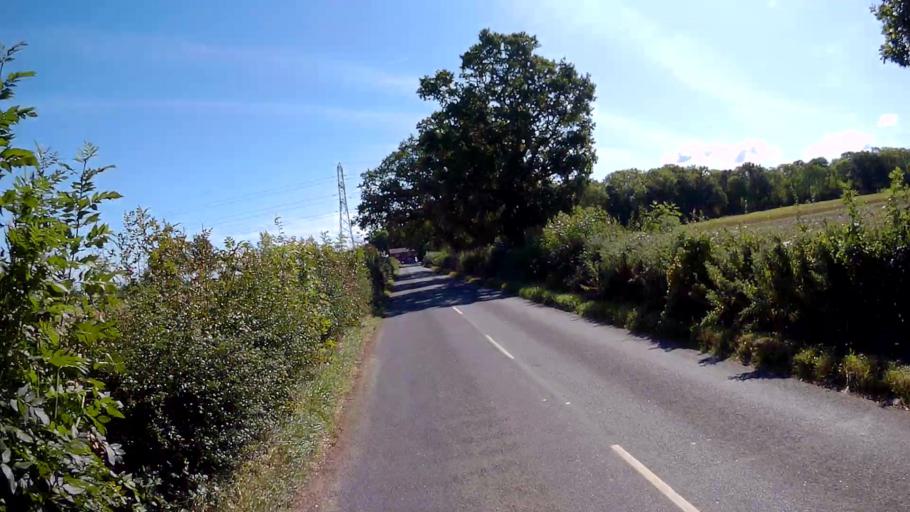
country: GB
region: England
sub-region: West Berkshire
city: Stratfield Mortimer
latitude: 51.3715
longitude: -1.0317
